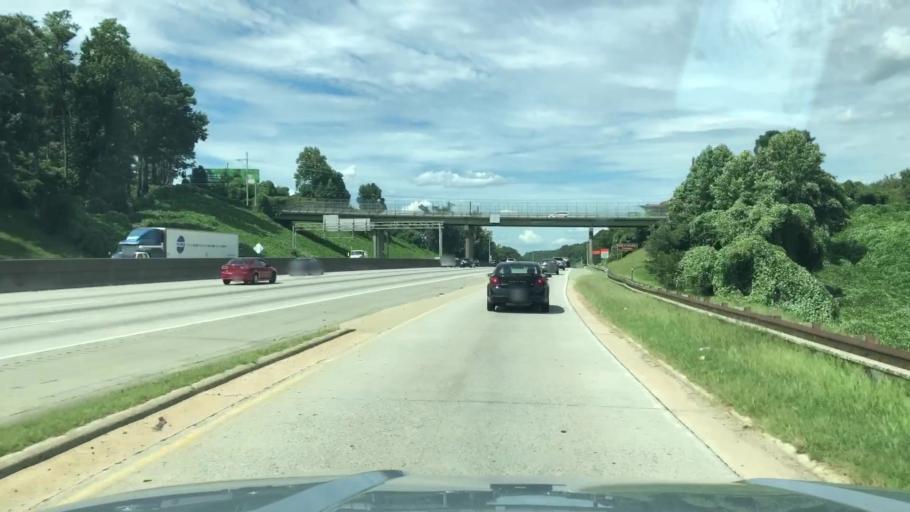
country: US
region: Georgia
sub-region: Fulton County
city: College Park
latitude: 33.6591
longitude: -84.4973
